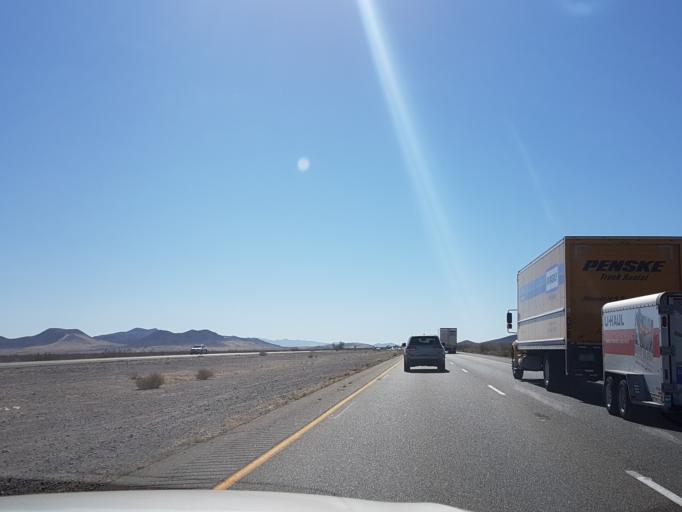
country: US
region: California
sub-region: San Bernardino County
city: Fort Irwin
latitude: 35.1723
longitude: -116.1762
